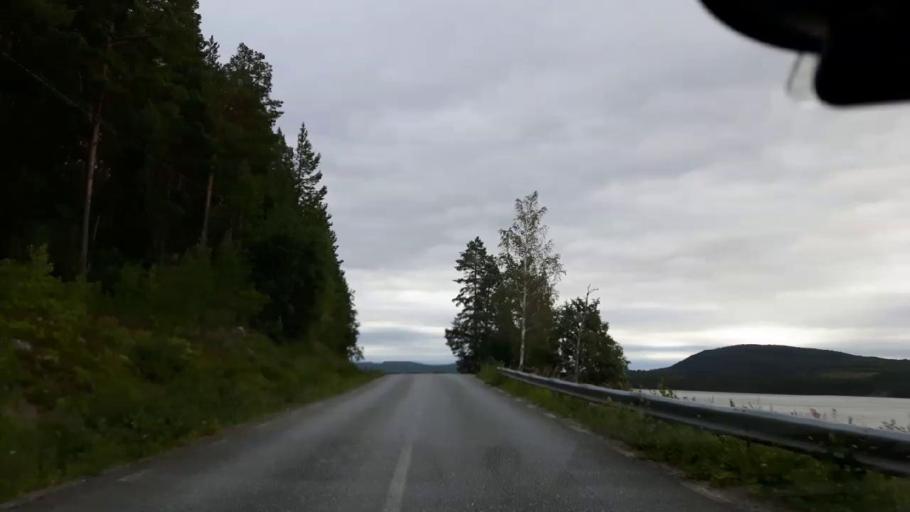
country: SE
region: Jaemtland
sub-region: Braecke Kommun
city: Braecke
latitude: 62.8653
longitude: 15.6182
